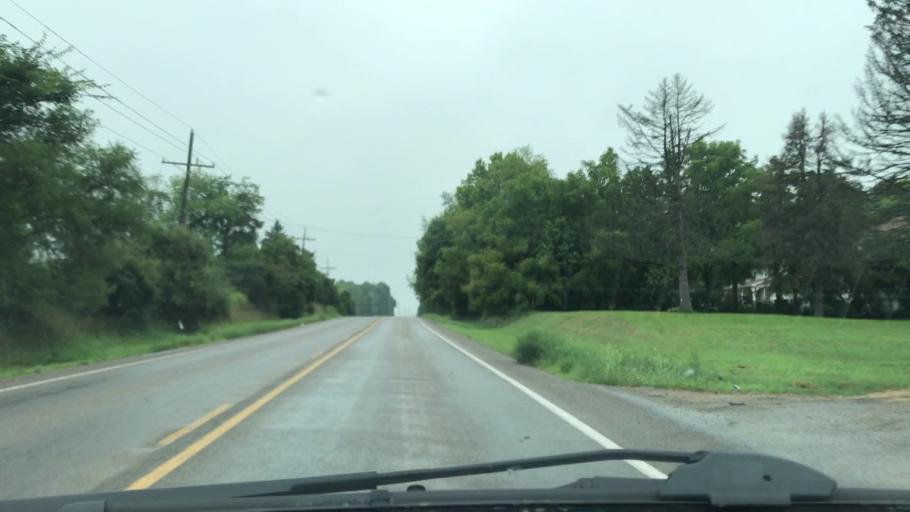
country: US
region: Indiana
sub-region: Hamilton County
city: Westfield
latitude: 40.0996
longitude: -86.1402
